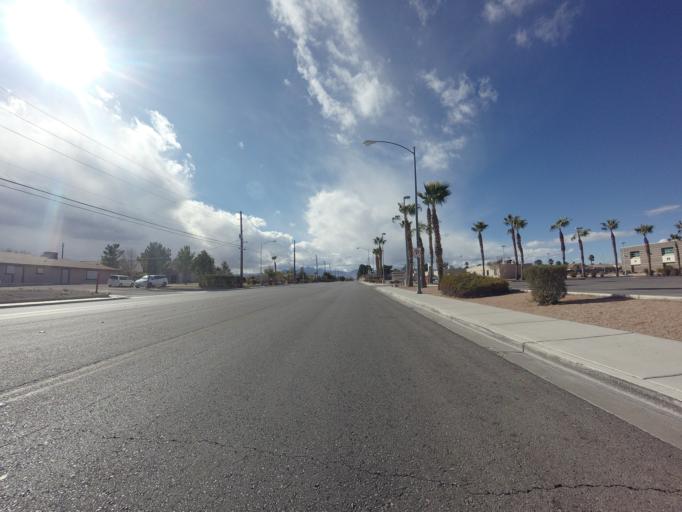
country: US
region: Nevada
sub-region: Clark County
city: North Las Vegas
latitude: 36.2543
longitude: -115.1376
